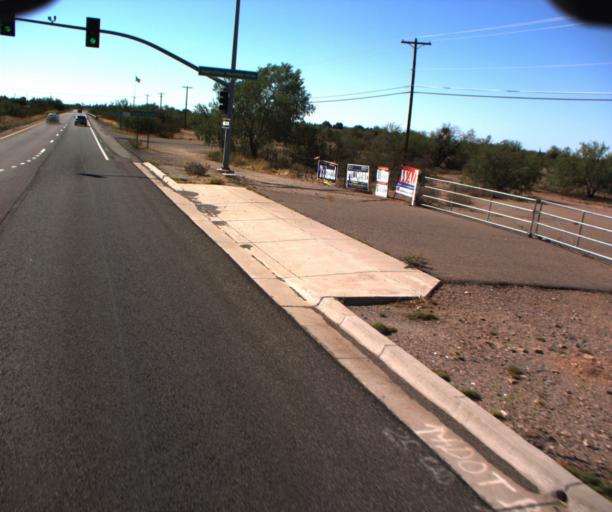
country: US
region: Arizona
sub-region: Pinal County
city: Apache Junction
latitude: 33.3666
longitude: -111.4781
